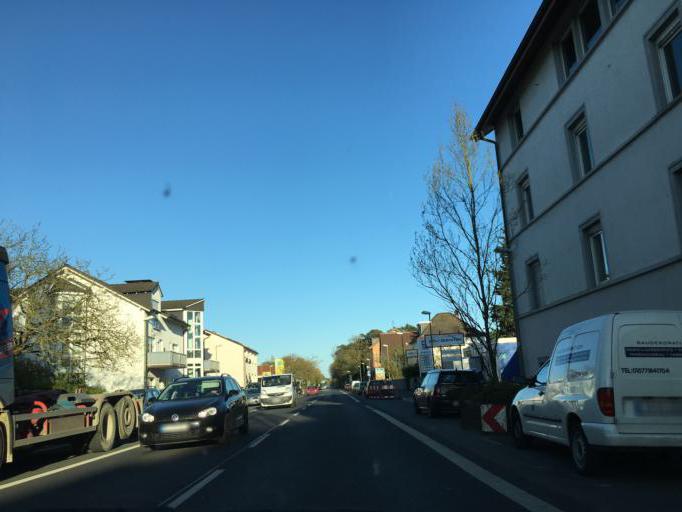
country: DE
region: Hesse
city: Heusenstamm
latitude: 50.0842
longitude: 8.8175
